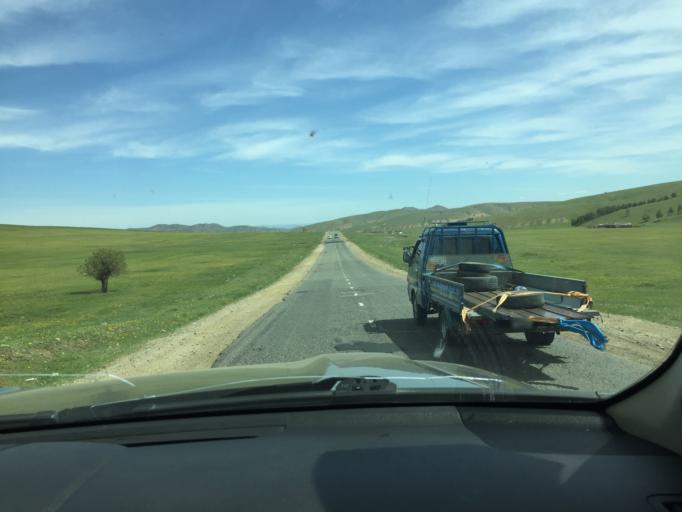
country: MN
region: Central Aimak
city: Javhlant
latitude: 48.6552
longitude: 106.1128
